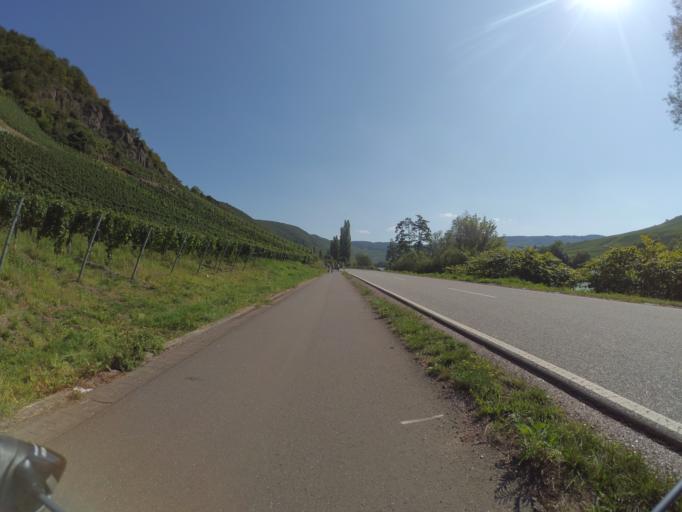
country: DE
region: Rheinland-Pfalz
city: Trittenheim
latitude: 49.8358
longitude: 6.8995
